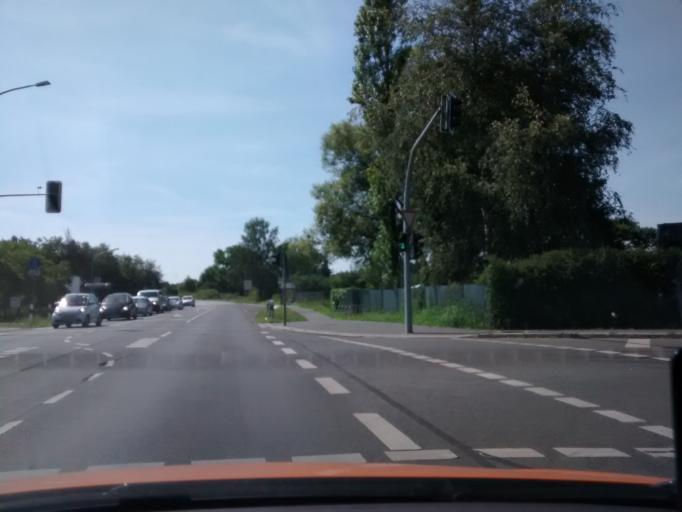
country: DE
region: Brandenburg
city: Hohen Neuendorf
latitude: 52.6575
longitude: 13.2562
